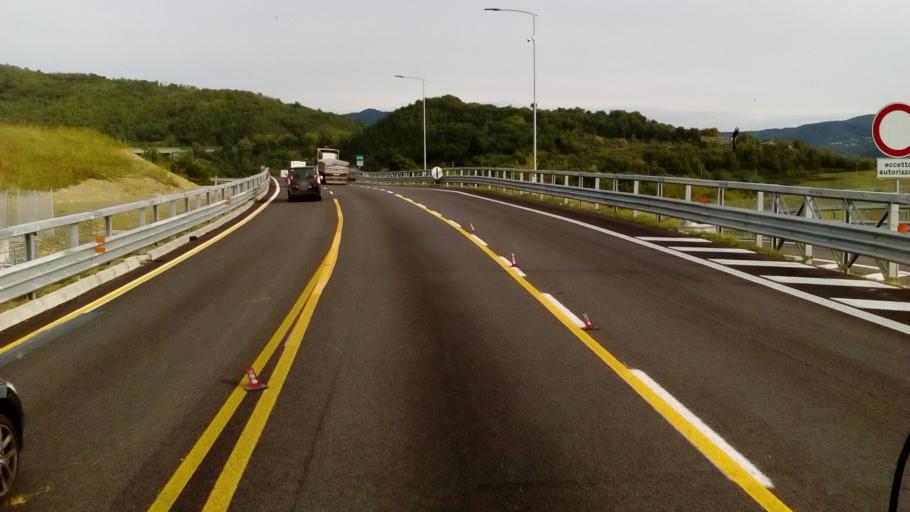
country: IT
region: Tuscany
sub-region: Province of Florence
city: Barberino di Mugello
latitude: 44.0309
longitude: 11.2263
